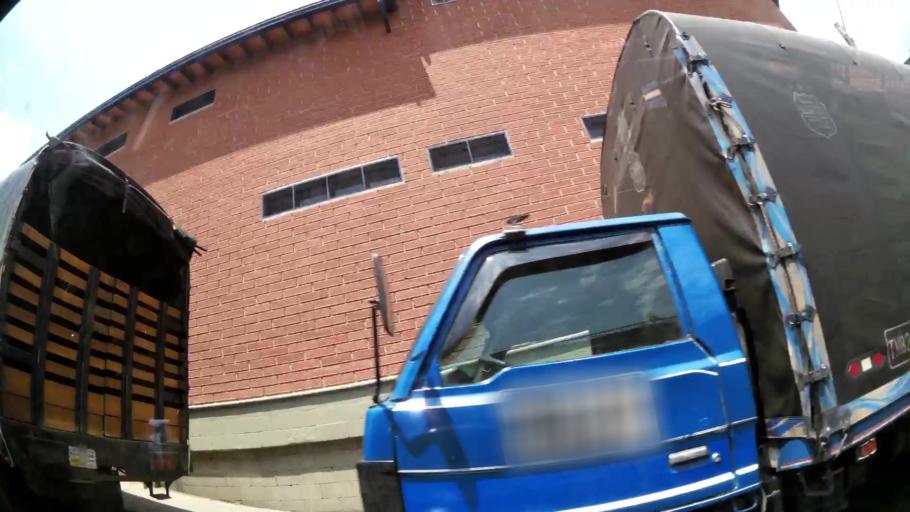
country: CO
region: Antioquia
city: Medellin
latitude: 6.2901
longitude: -75.5752
